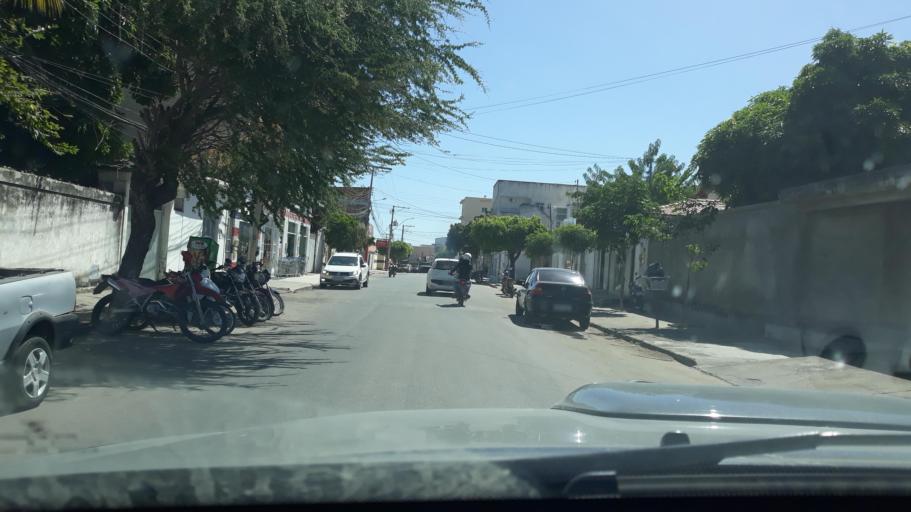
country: BR
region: Bahia
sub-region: Guanambi
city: Guanambi
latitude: -14.2246
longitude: -42.7896
